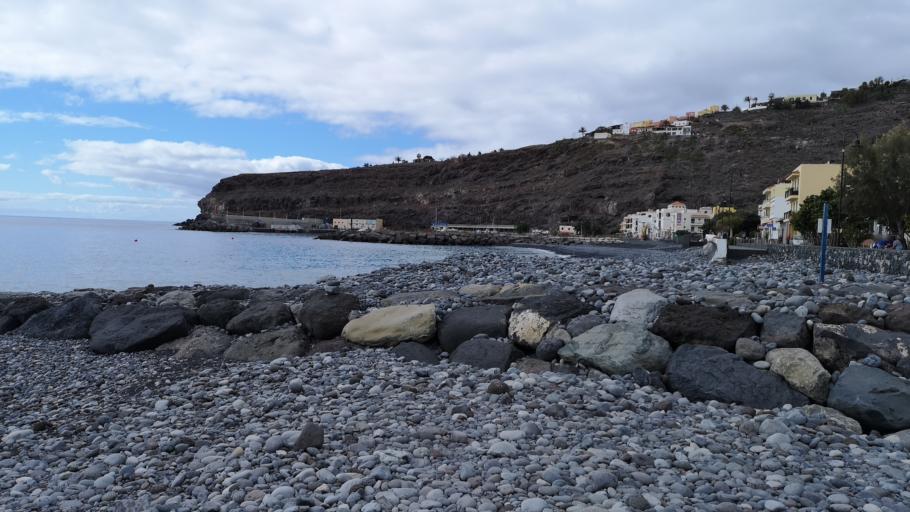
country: ES
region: Canary Islands
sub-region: Provincia de Santa Cruz de Tenerife
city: Alajero
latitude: 28.0294
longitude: -17.1944
